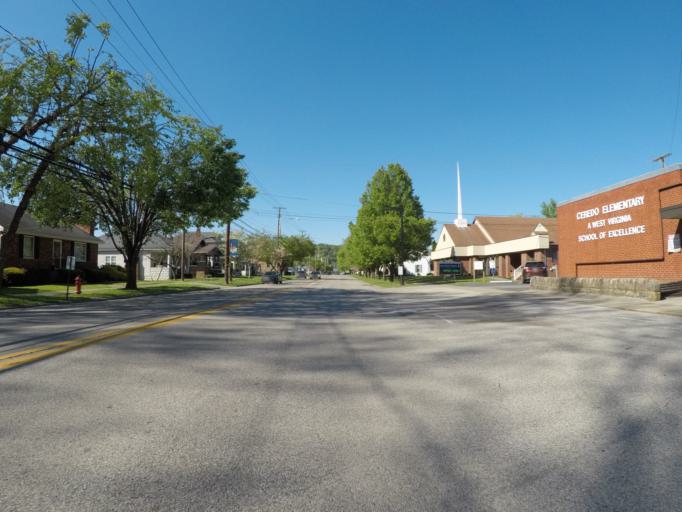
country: US
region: West Virginia
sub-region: Wayne County
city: Ceredo
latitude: 38.3941
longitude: -82.5592
